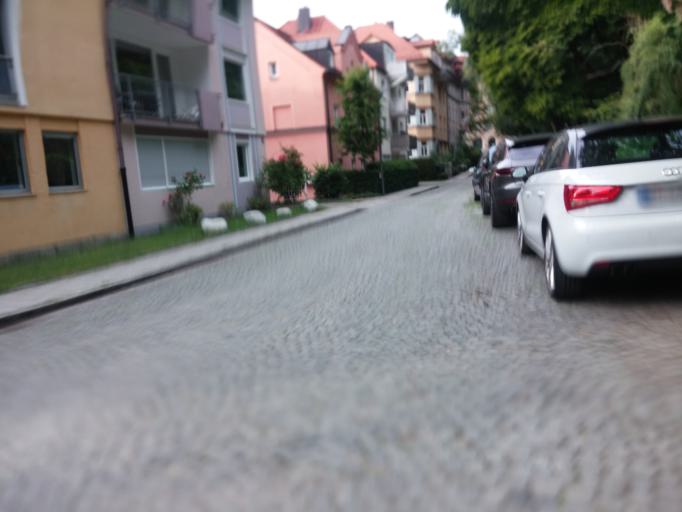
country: DE
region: Bavaria
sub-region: Upper Bavaria
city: Bogenhausen
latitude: 48.1480
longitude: 11.6001
